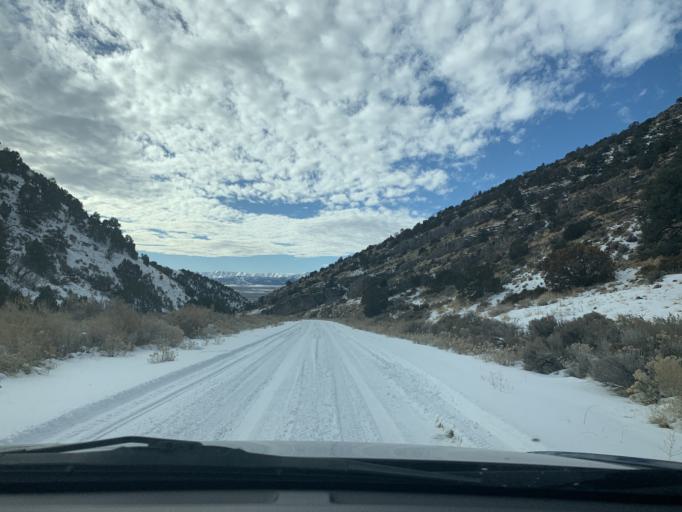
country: US
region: Utah
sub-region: Tooele County
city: Tooele
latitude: 40.3124
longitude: -112.2433
